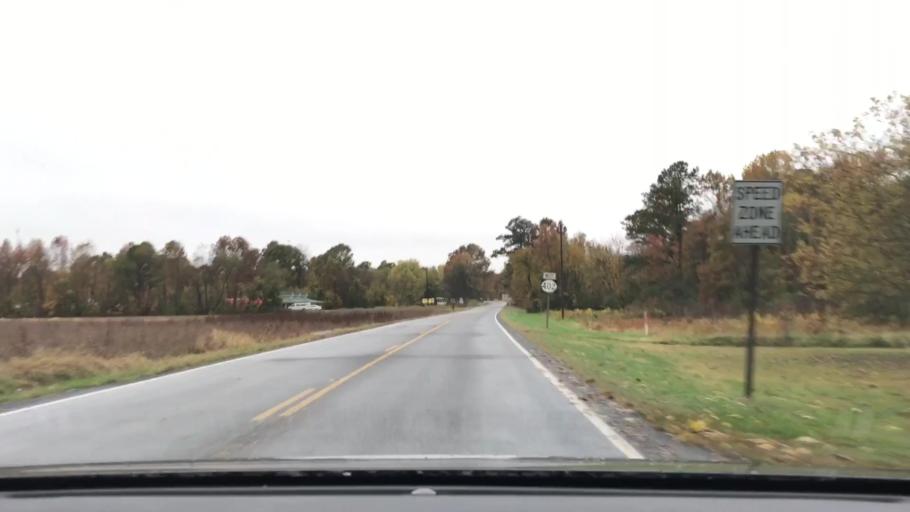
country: US
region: Kentucky
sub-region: Marshall County
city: Benton
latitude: 36.7677
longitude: -88.2966
